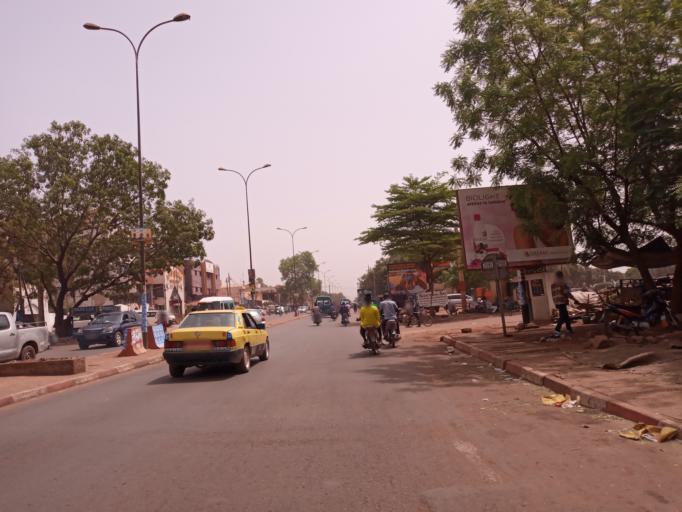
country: ML
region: Bamako
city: Bamako
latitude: 12.6538
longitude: -7.9795
